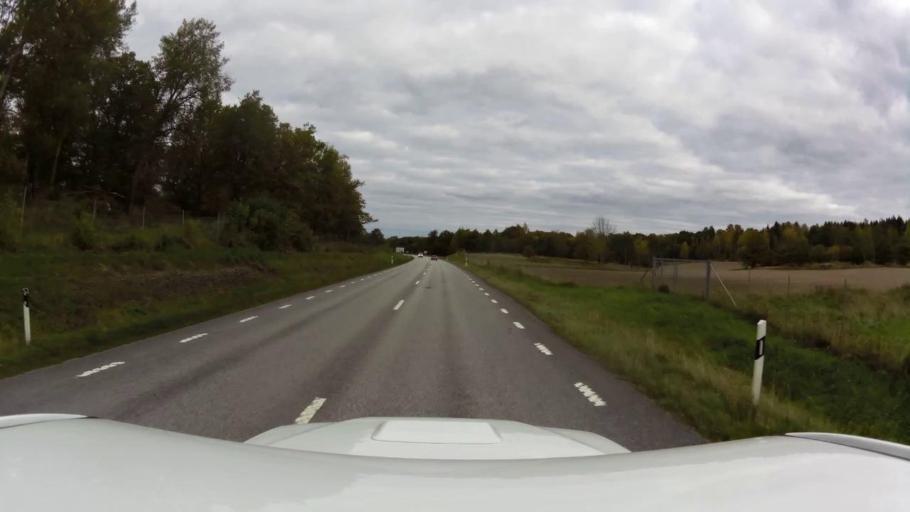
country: SE
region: OEstergoetland
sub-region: Kinda Kommun
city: Rimforsa
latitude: 58.2075
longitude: 15.6689
